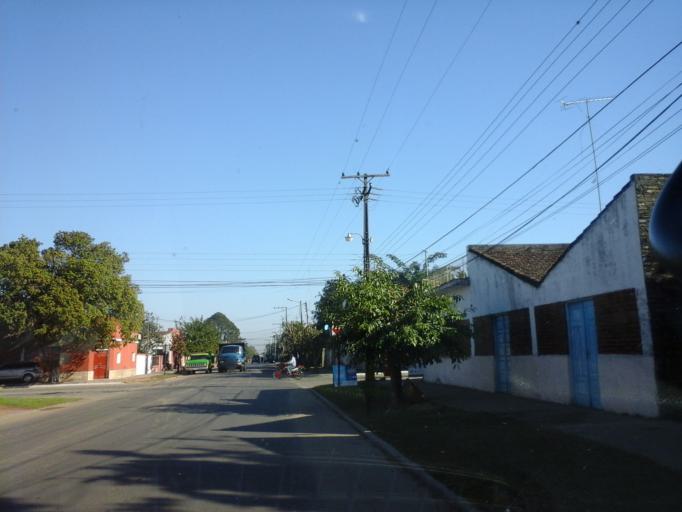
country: PY
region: Neembucu
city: Pilar
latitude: -26.8634
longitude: -58.3014
